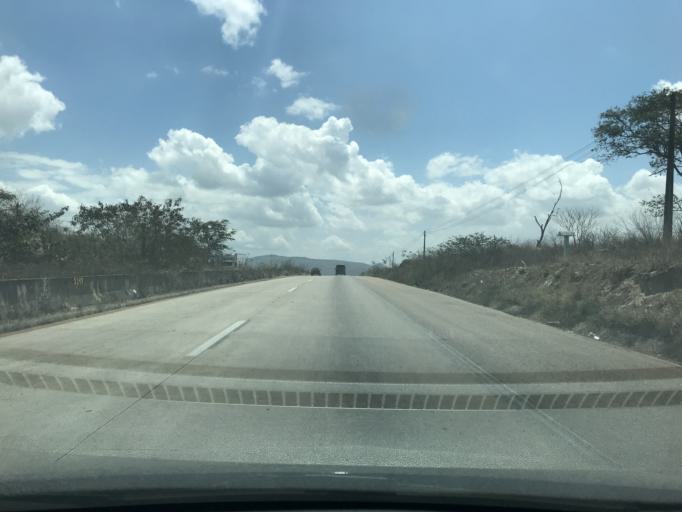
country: BR
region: Pernambuco
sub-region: Bezerros
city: Bezerros
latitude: -8.2970
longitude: -35.8302
